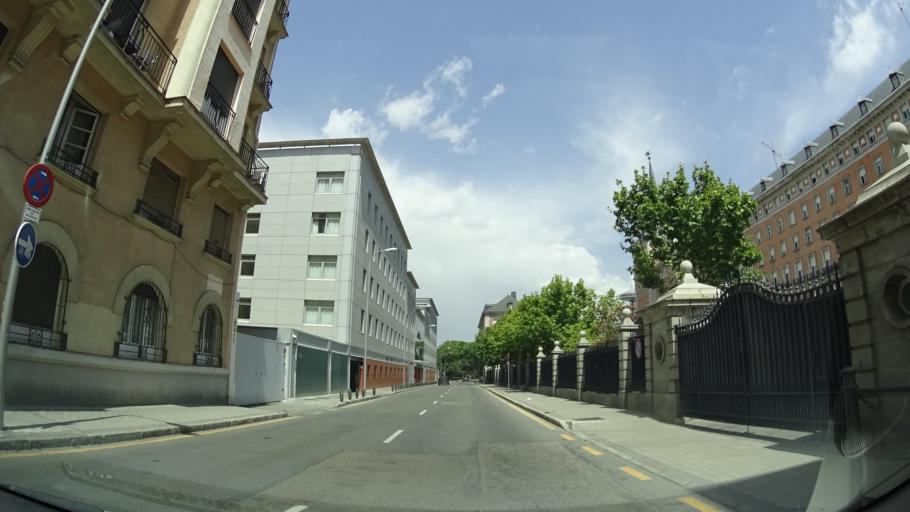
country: ES
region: Madrid
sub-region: Provincia de Madrid
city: Moncloa-Aravaca
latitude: 40.4327
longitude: -3.7207
